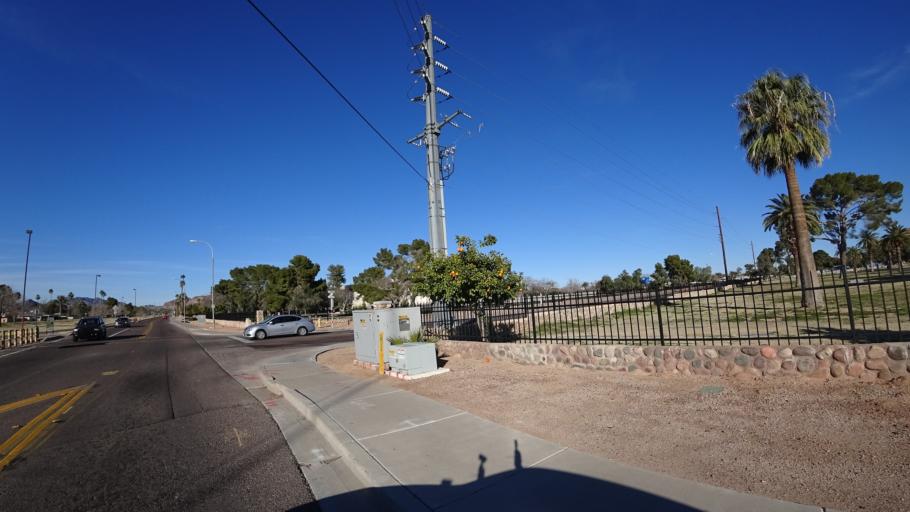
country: US
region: Arizona
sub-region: Maricopa County
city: Tempe Junction
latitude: 33.4726
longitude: -111.9781
